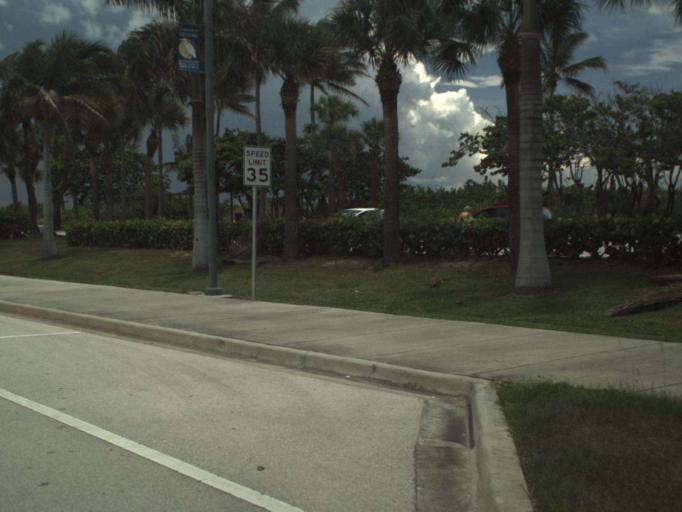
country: US
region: Florida
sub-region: Saint Lucie County
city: Fort Pierce
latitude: 27.4538
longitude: -80.2861
